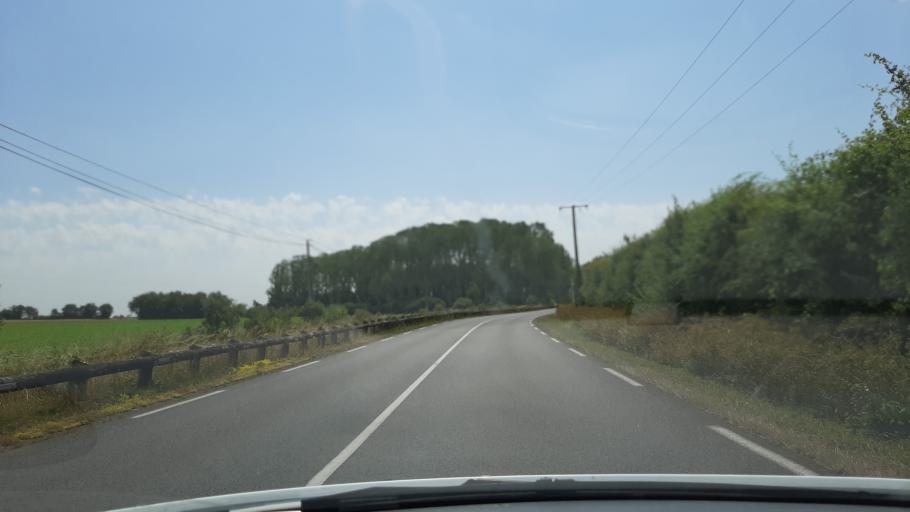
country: FR
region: Pays de la Loire
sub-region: Departement de la Vendee
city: Le Poire-sur-Vie
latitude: 46.7581
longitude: -1.4767
